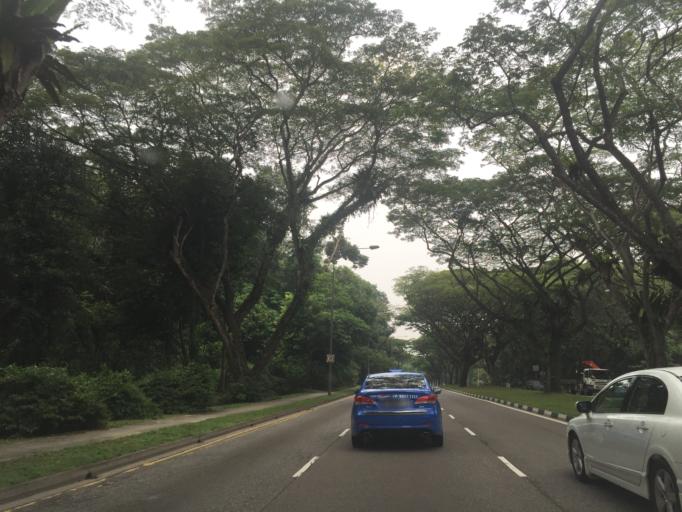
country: SG
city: Singapore
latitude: 1.3865
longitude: 103.8212
